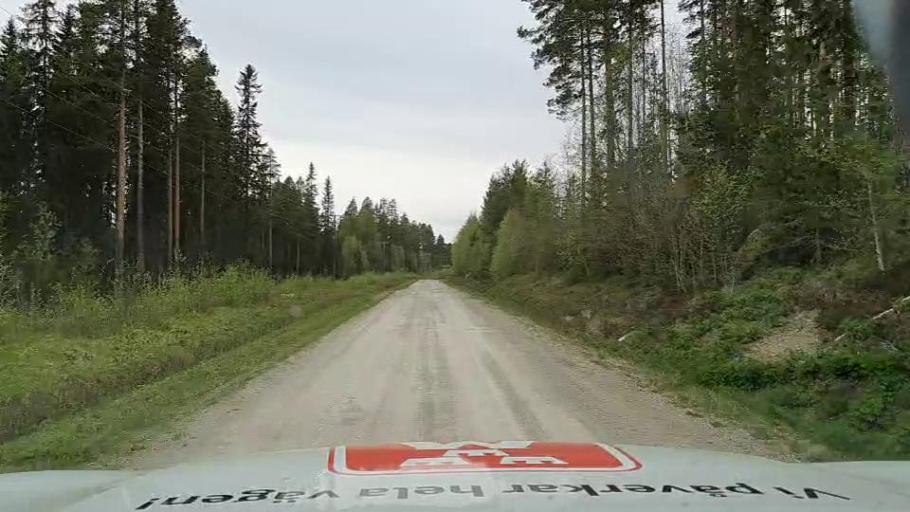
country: SE
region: Jaemtland
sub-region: Bergs Kommun
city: Hoverberg
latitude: 62.6738
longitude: 14.8028
